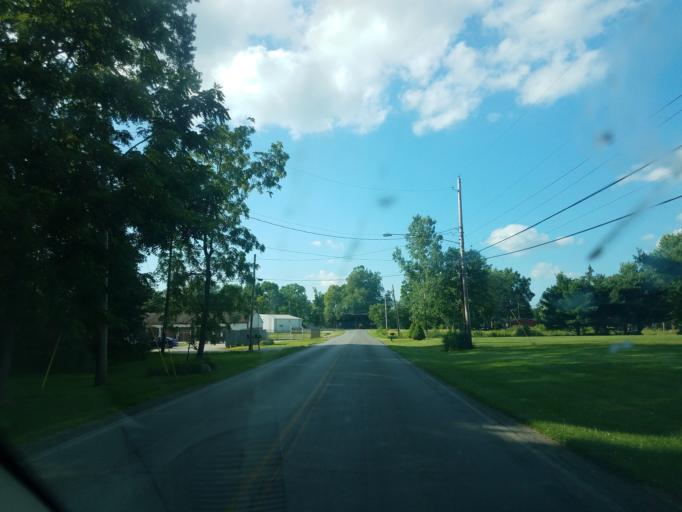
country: US
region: Ohio
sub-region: Wayne County
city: Apple Creek
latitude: 40.7615
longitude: -81.8960
